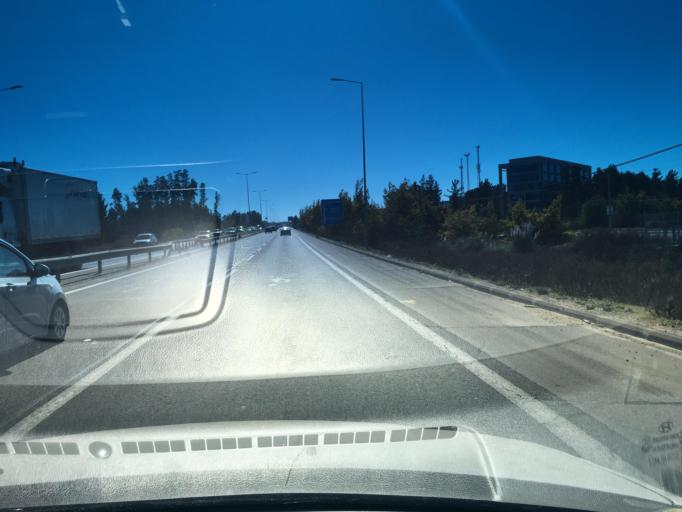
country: CL
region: Valparaiso
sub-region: Provincia de Valparaiso
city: Vina del Mar
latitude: -33.1349
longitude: -71.5625
